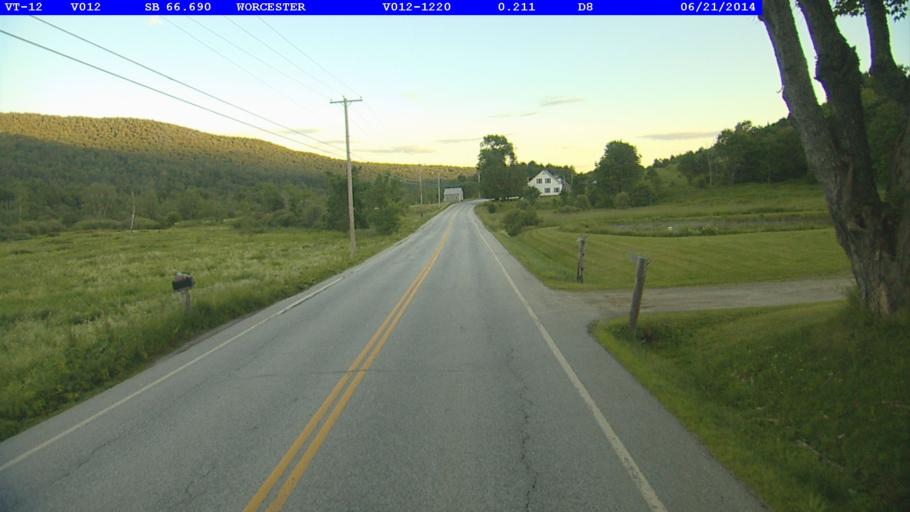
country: US
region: Vermont
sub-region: Washington County
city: Montpelier
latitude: 44.3557
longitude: -72.5648
